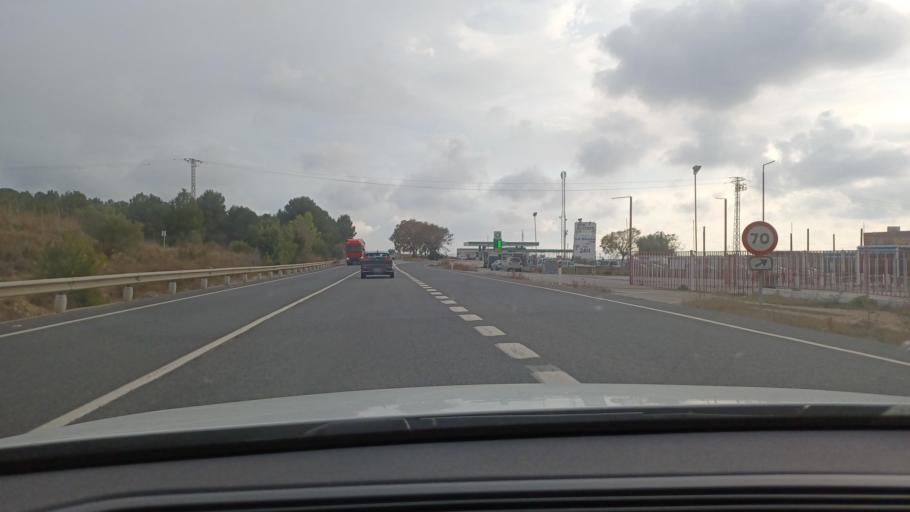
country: ES
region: Catalonia
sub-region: Provincia de Tarragona
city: la Pobla de Mafumet
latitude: 41.1758
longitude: 1.2403
